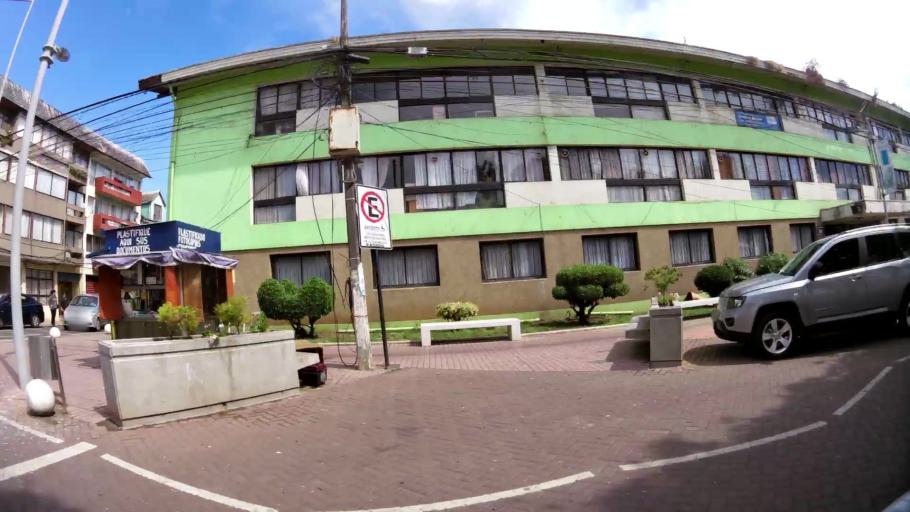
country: CL
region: Biobio
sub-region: Provincia de Concepcion
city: Talcahuano
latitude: -36.7145
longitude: -73.1147
